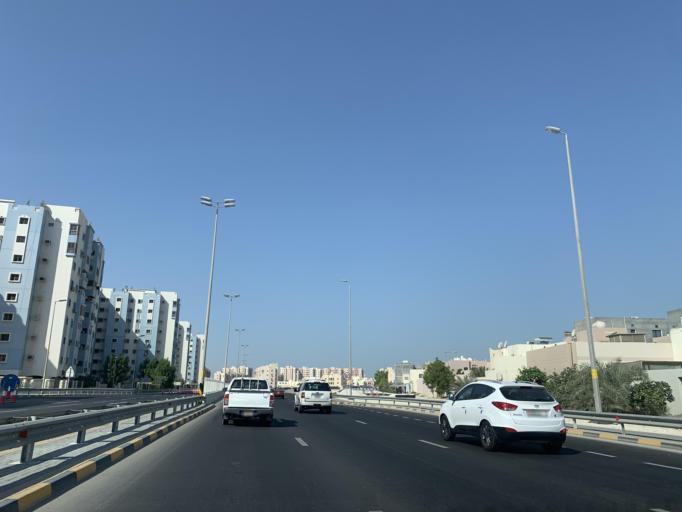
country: BH
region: Central Governorate
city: Madinat Hamad
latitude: 26.1140
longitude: 50.4925
